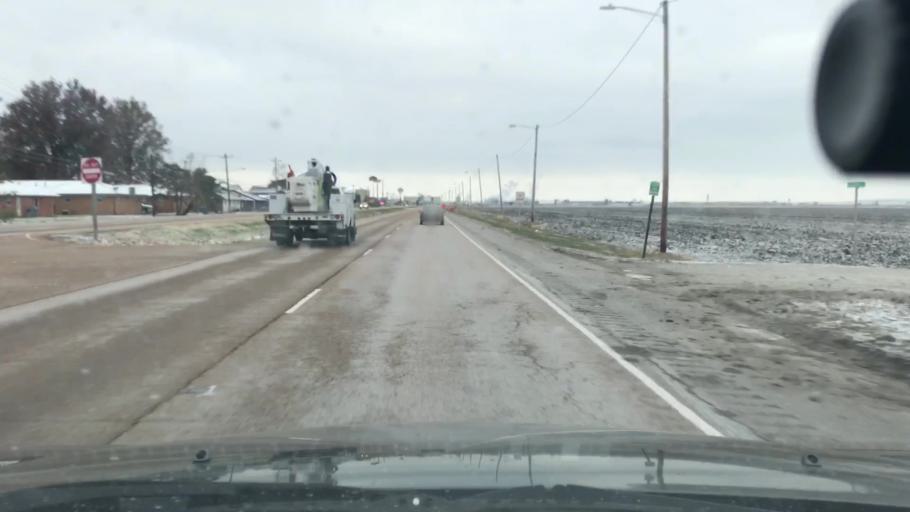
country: US
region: Illinois
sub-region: Madison County
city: Pontoon Beach
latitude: 38.7393
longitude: -90.0710
